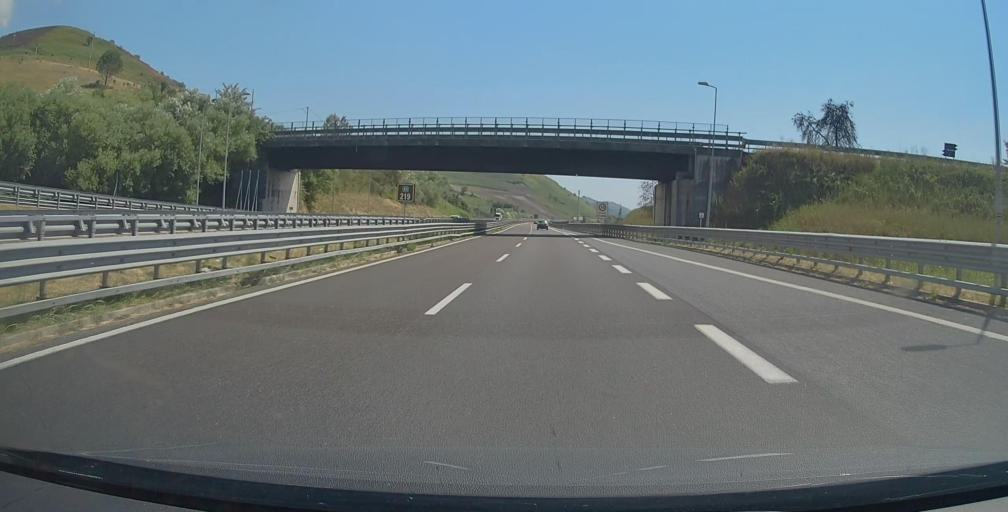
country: IT
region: Calabria
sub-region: Provincia di Vibo-Valentia
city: Francica
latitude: 38.6239
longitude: 16.1604
